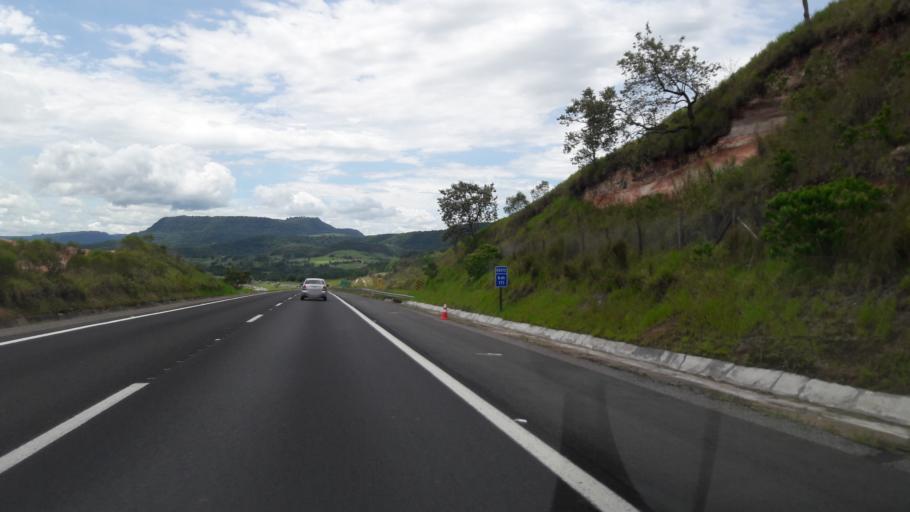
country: BR
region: Sao Paulo
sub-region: Porangaba
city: Porangaba
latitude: -23.2106
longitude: -48.2029
